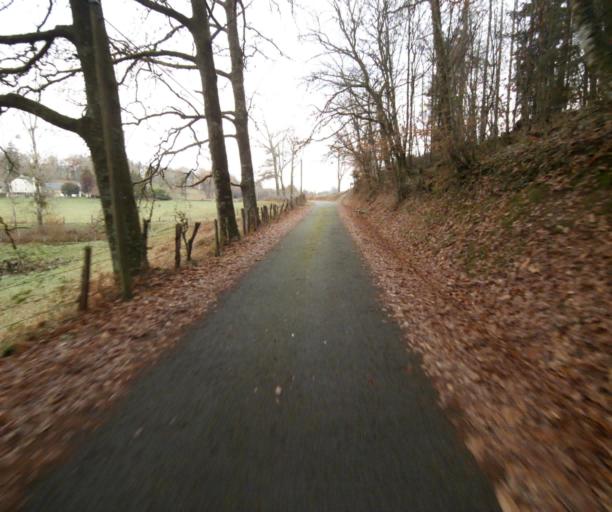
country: FR
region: Limousin
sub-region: Departement de la Correze
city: Chameyrat
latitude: 45.2267
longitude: 1.6974
